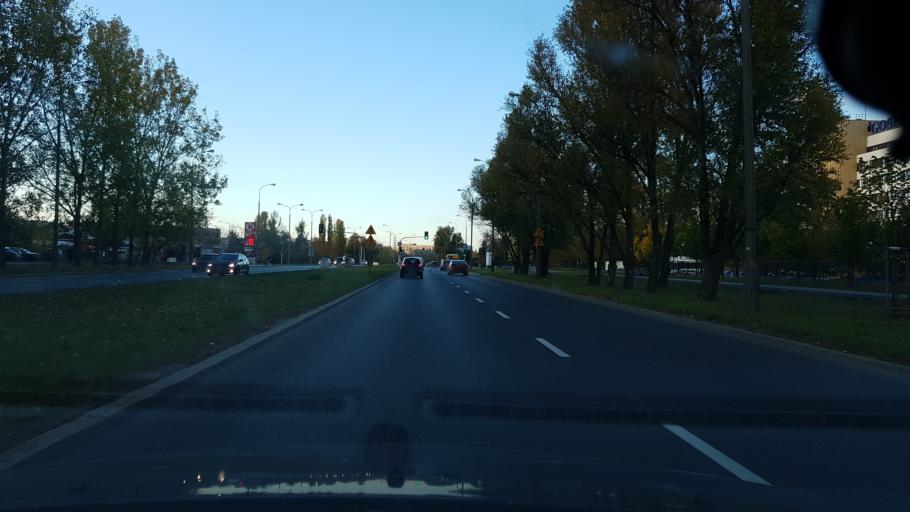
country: PL
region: Masovian Voivodeship
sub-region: Warszawa
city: Ursynow
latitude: 52.1614
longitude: 21.0391
